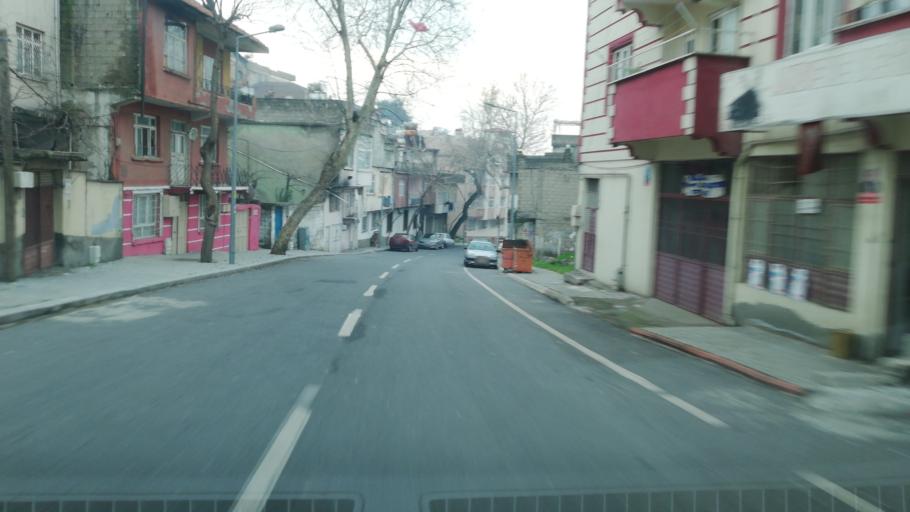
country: TR
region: Kahramanmaras
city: Kahramanmaras
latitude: 37.5923
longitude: 36.9266
